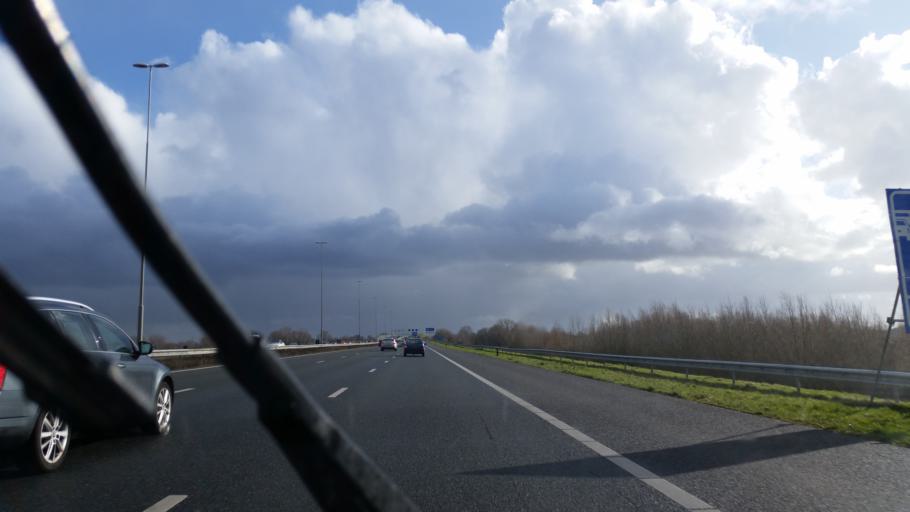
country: NL
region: Gelderland
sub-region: Gemeente Maasdriel
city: Hedel
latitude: 51.7464
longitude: 5.2959
